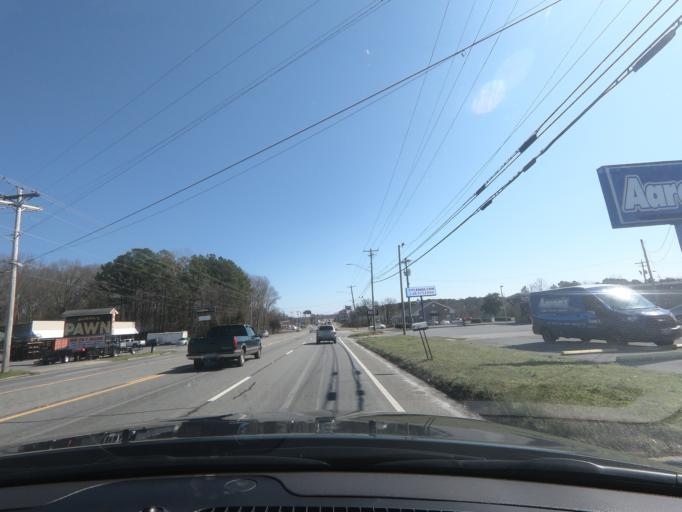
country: US
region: Georgia
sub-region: Gordon County
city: Calhoun
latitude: 34.4772
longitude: -84.9318
